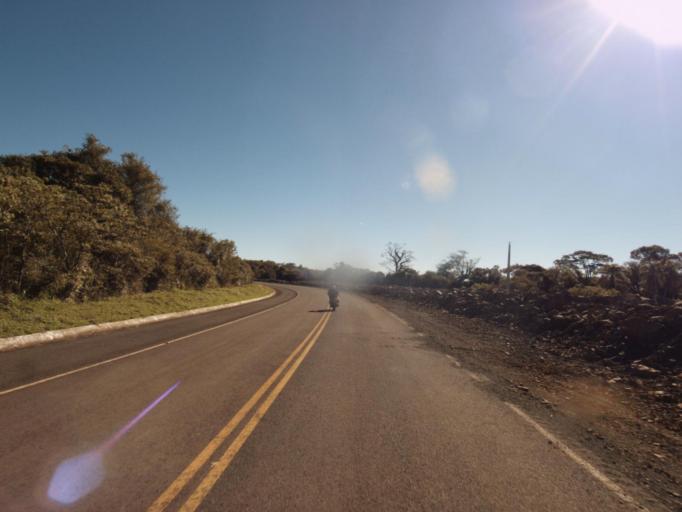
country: AR
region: Misiones
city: Bernardo de Irigoyen
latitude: -26.6132
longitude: -53.6987
